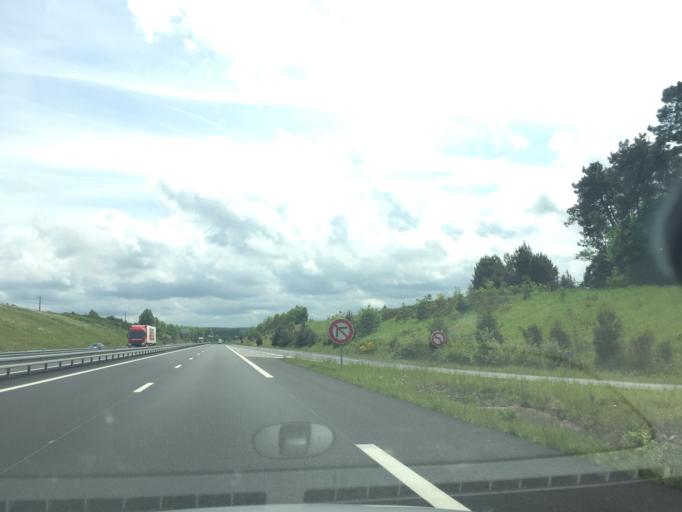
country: FR
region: Pays de la Loire
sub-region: Departement de la Sarthe
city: Ecommoy
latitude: 47.8204
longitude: 0.3069
